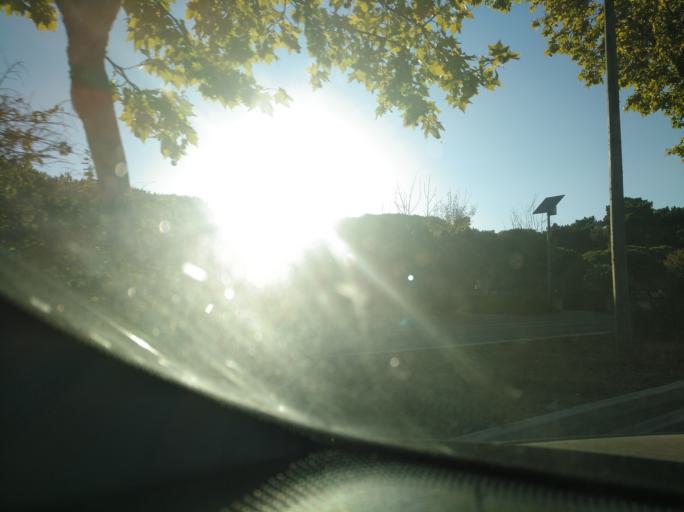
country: PT
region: Faro
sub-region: Vila Real de Santo Antonio
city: Vila Real de Santo Antonio
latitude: 37.1889
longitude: -7.4230
